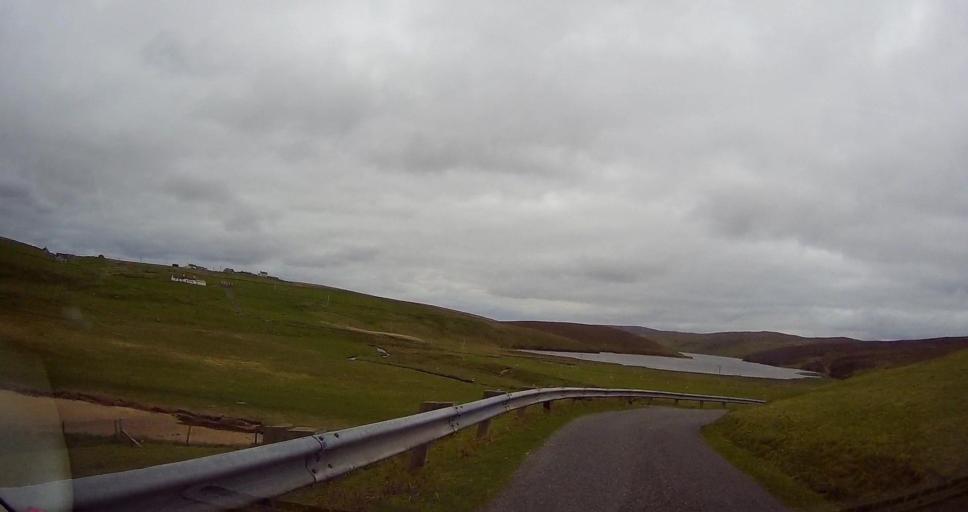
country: GB
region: Scotland
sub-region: Shetland Islands
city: Shetland
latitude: 60.8060
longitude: -0.8810
